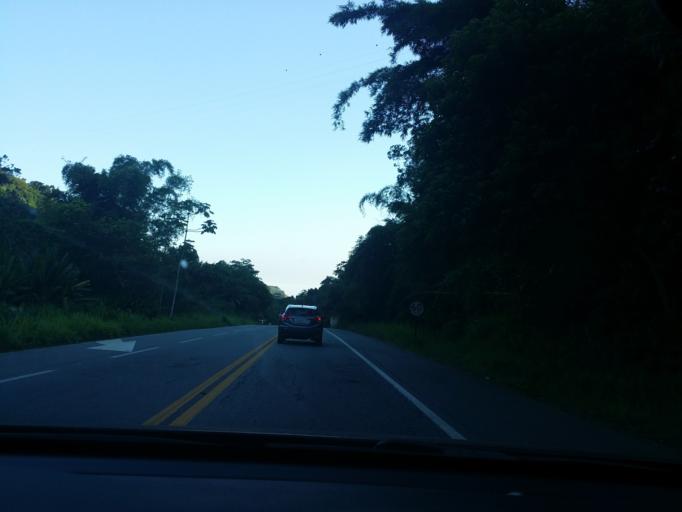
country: BR
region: Sao Paulo
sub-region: Sao Sebastiao
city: Sao Sebastiao
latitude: -23.7446
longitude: -45.7293
